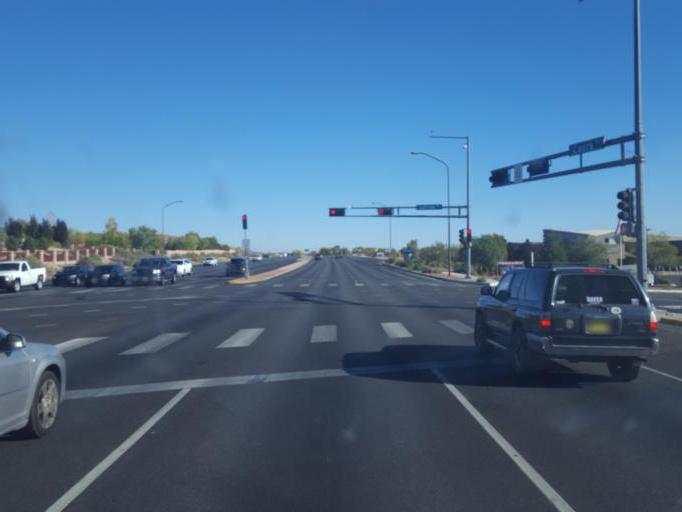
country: US
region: New Mexico
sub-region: Bernalillo County
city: Lee Acres
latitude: 35.1597
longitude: -106.6793
